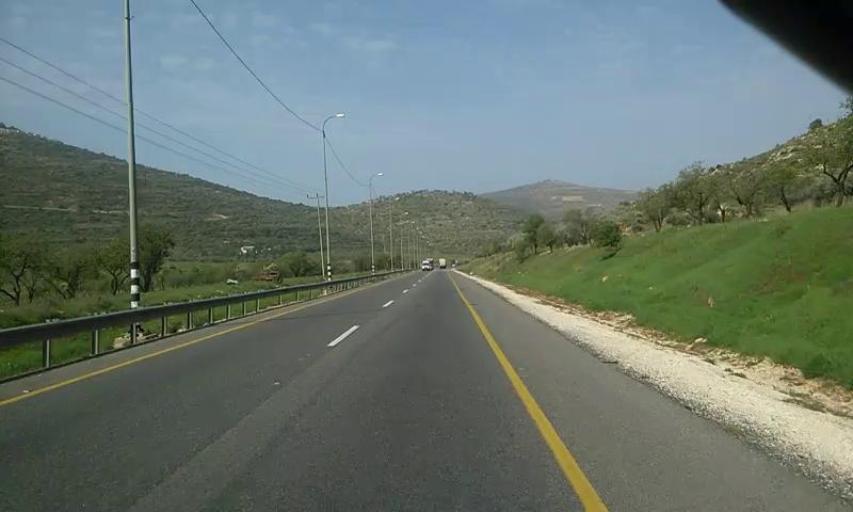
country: PS
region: West Bank
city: Al Lubban ash Sharqiyah
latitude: 32.0636
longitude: 35.2495
